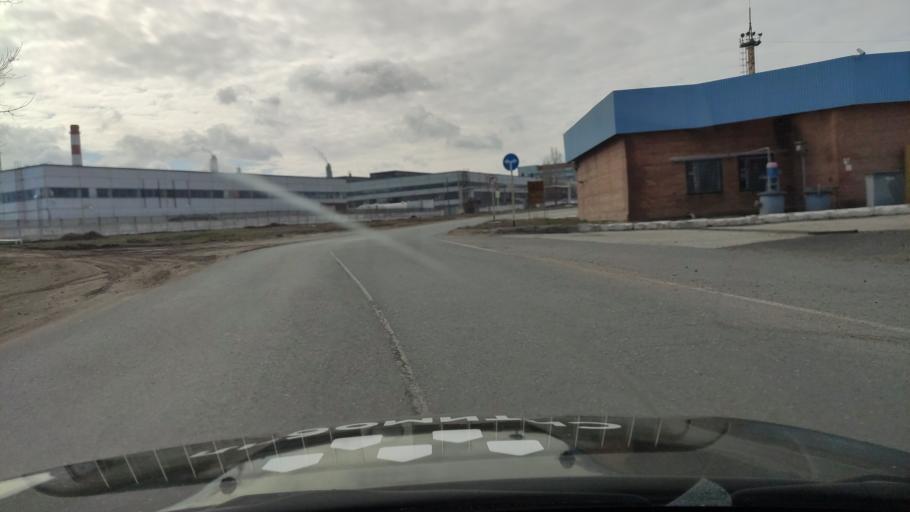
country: RU
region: Samara
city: Povolzhskiy
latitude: 53.5509
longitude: 49.6175
